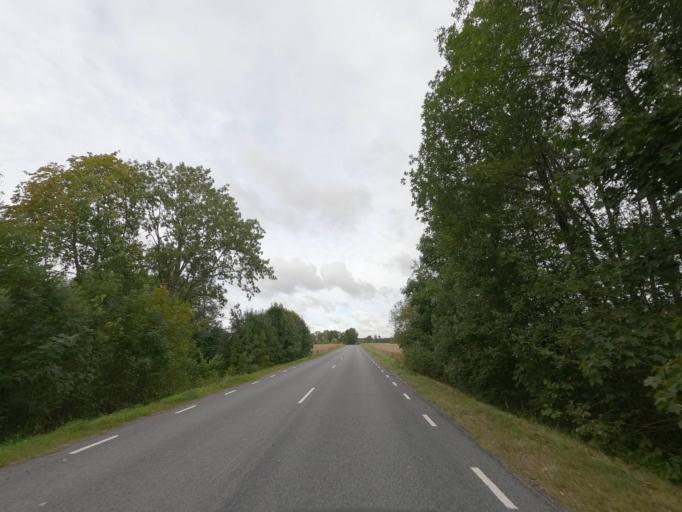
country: EE
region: Raplamaa
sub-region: Maerjamaa vald
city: Marjamaa
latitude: 59.0092
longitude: 24.5728
